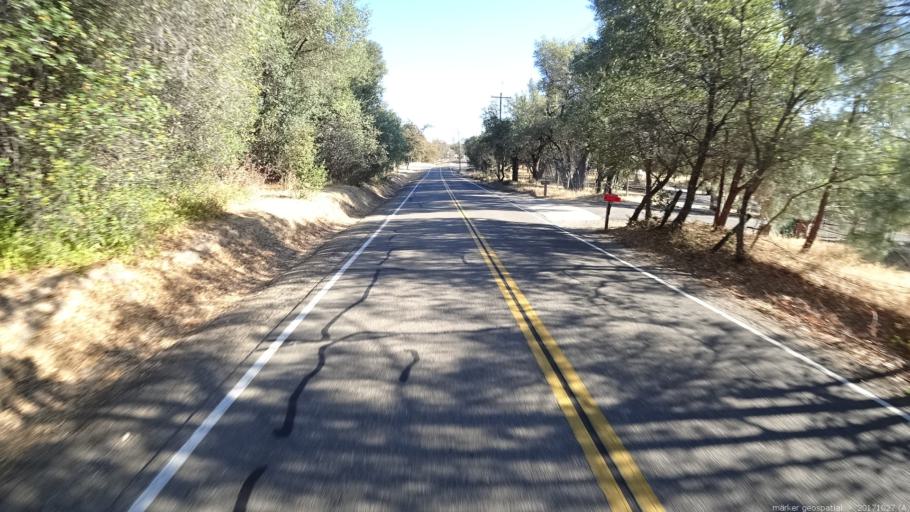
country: US
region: California
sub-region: Shasta County
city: Palo Cedro
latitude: 40.5579
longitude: -122.1867
